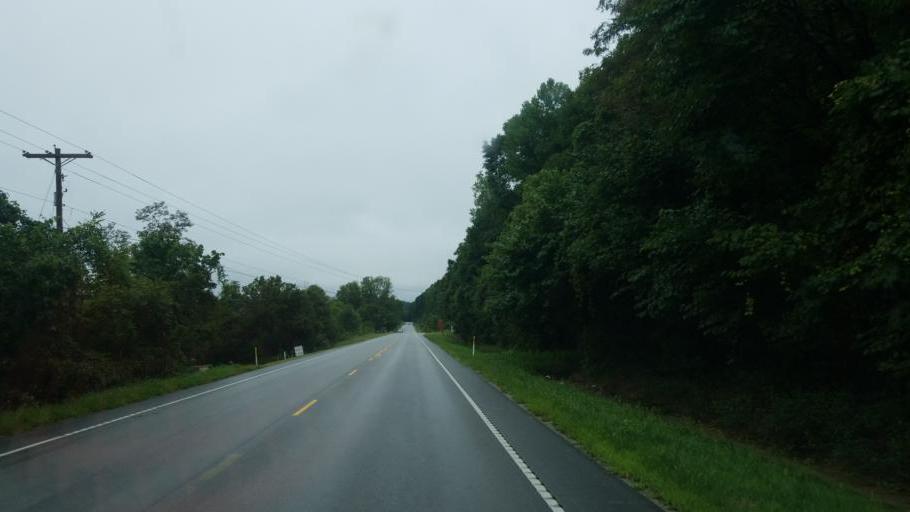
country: US
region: Ohio
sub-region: Adams County
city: Manchester
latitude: 38.6665
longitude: -83.6384
